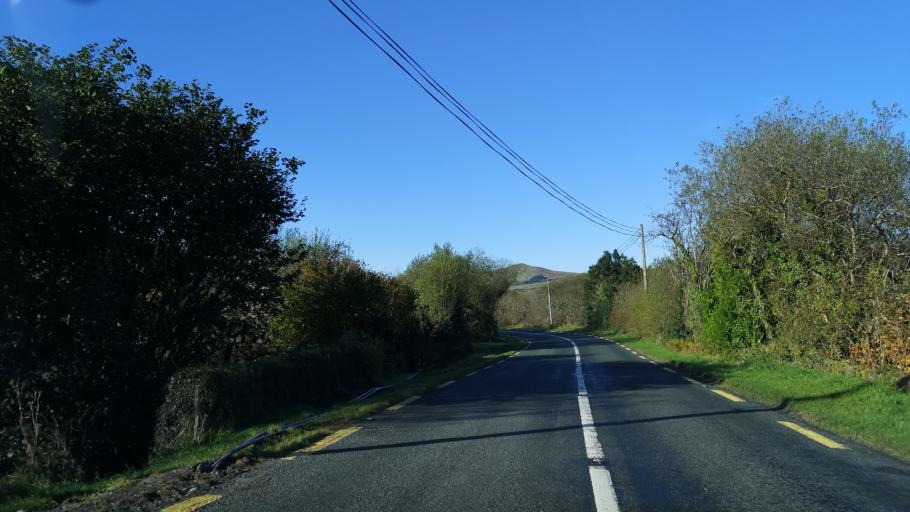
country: IE
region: Connaught
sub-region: Maigh Eo
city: Westport
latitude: 53.7102
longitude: -9.5585
